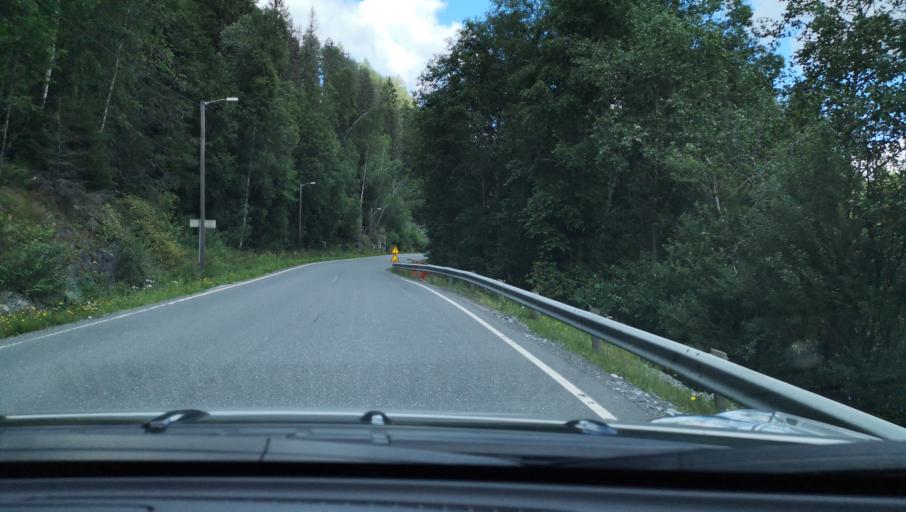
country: NO
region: Ostfold
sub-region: Hobol
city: Tomter
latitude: 59.6490
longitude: 10.9914
